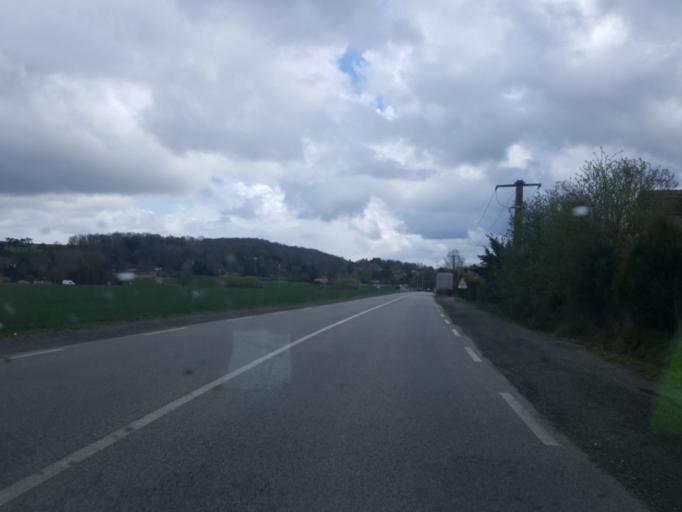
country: FR
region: Ile-de-France
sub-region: Departement du Val-d'Oise
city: Magny-en-Vexin
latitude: 49.1577
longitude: 1.7787
